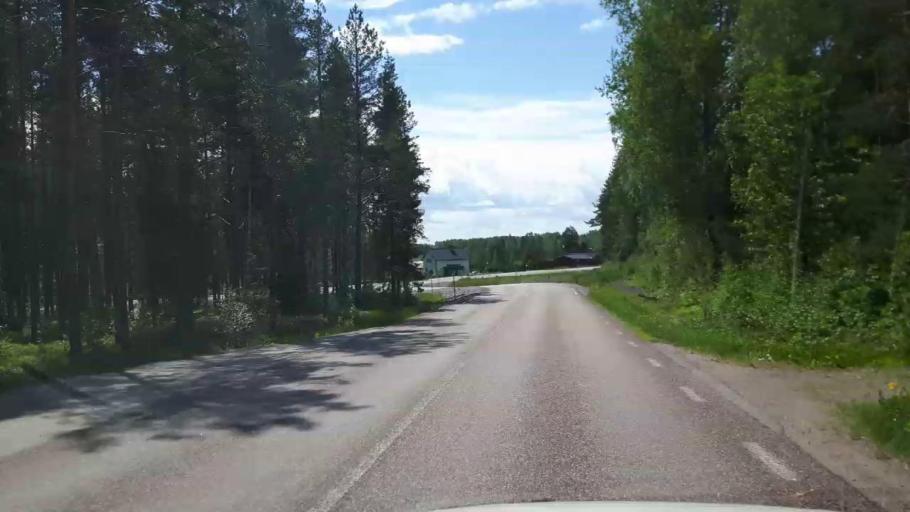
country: SE
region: Dalarna
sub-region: Faluns Kommun
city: Falun
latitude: 60.6169
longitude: 15.7645
